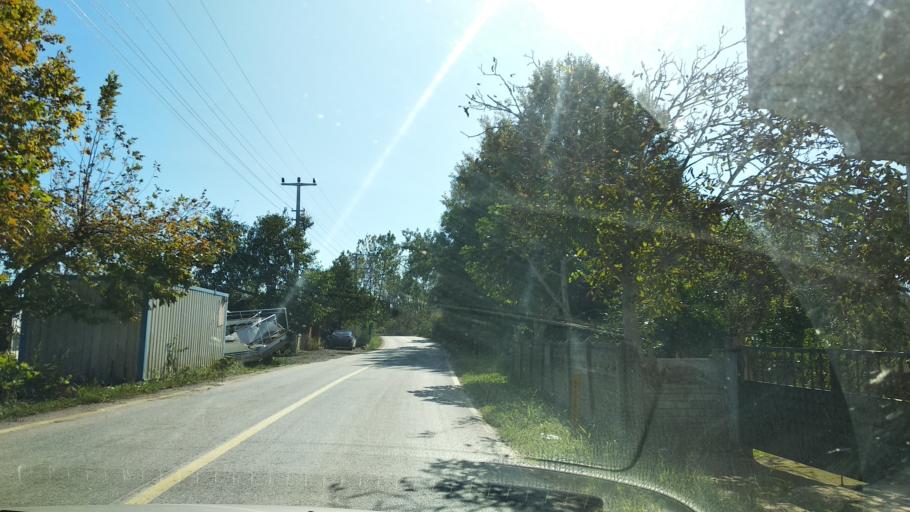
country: TR
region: Sakarya
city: Karasu
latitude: 41.1175
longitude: 30.6448
